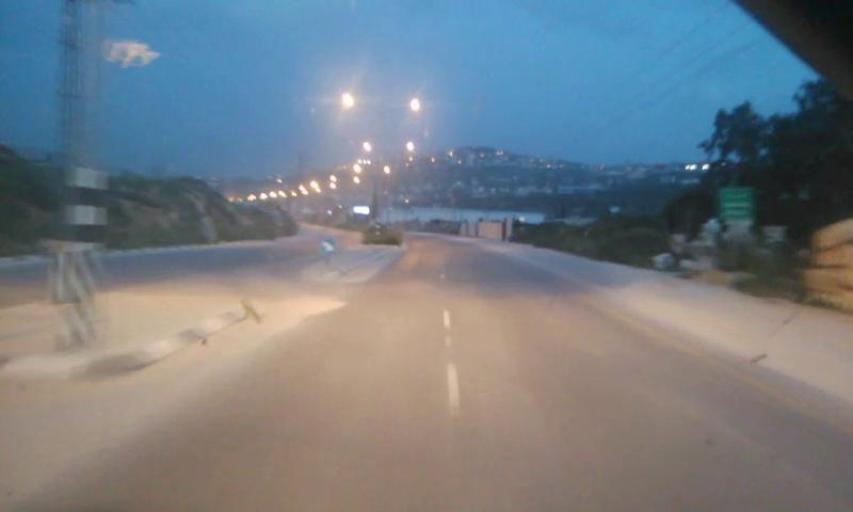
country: PS
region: West Bank
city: Dayr Sharaf
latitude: 32.2443
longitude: 35.1957
